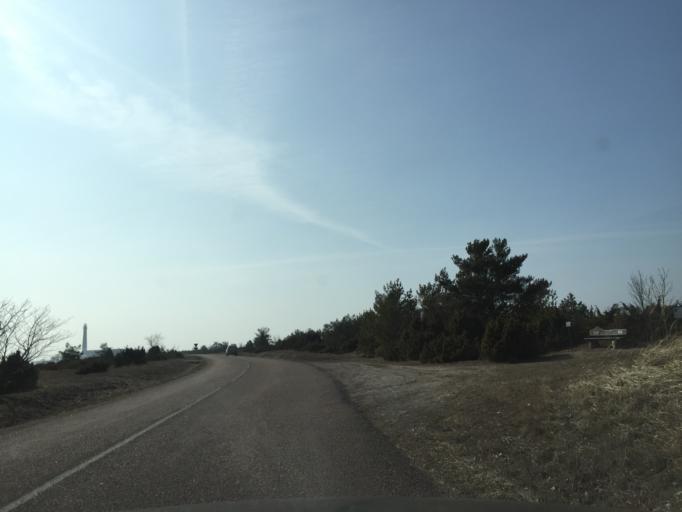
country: LV
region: Dundaga
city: Dundaga
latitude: 57.9176
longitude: 22.0637
